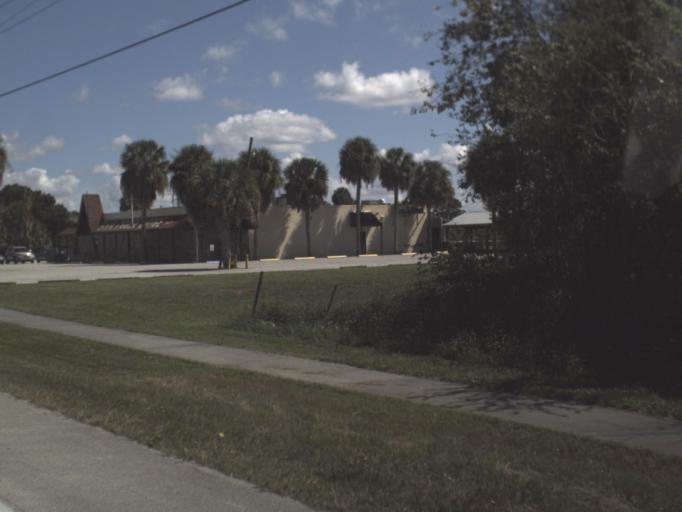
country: US
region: Florida
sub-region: Glades County
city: Buckhead Ridge
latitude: 27.1432
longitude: -80.8802
